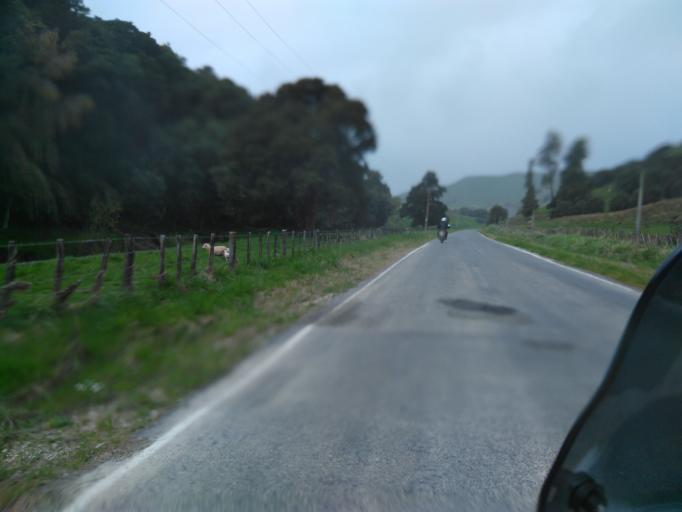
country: NZ
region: Gisborne
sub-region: Gisborne District
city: Gisborne
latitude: -38.6383
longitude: 177.7012
